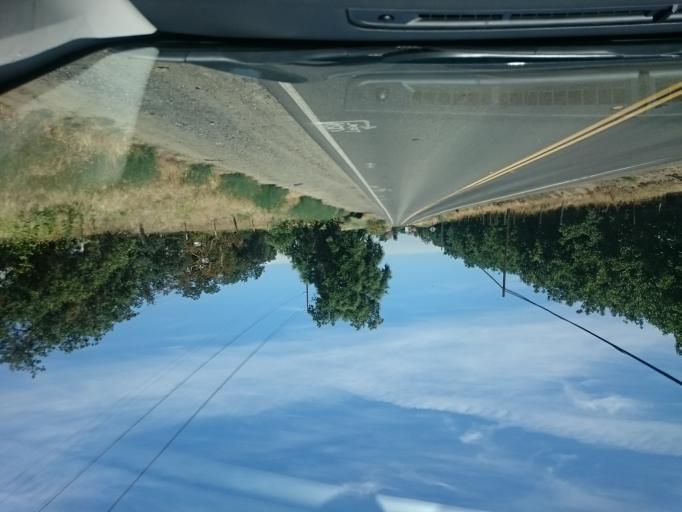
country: US
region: California
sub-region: Stanislaus County
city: Waterford
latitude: 37.6467
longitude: -120.6722
